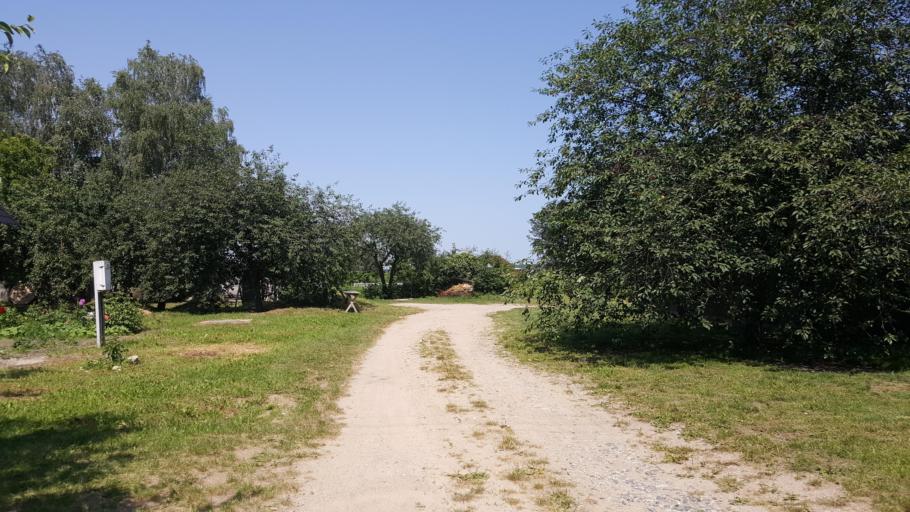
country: BY
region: Brest
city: Zhabinka
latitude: 52.1964
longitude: 23.9794
